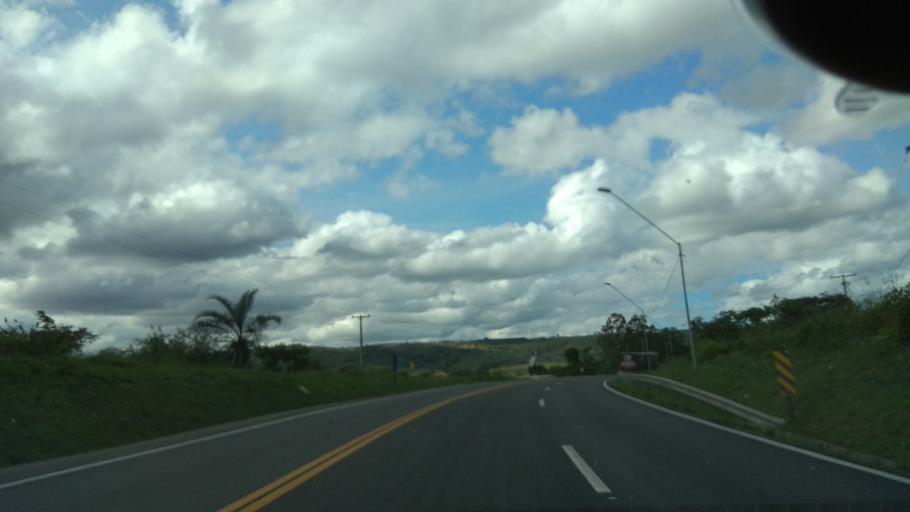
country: BR
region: Bahia
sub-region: Santa Ines
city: Santa Ines
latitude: -13.1048
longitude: -39.9939
